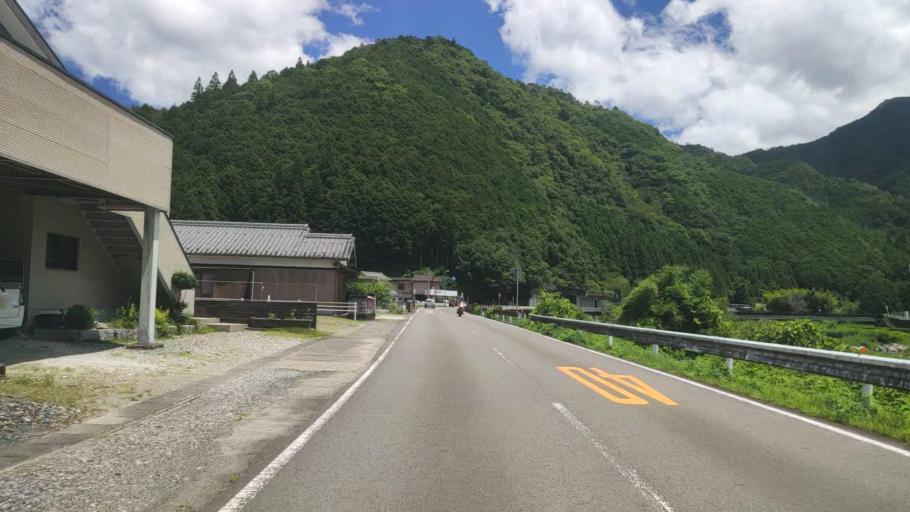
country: JP
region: Mie
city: Owase
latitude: 33.9852
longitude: 136.0438
